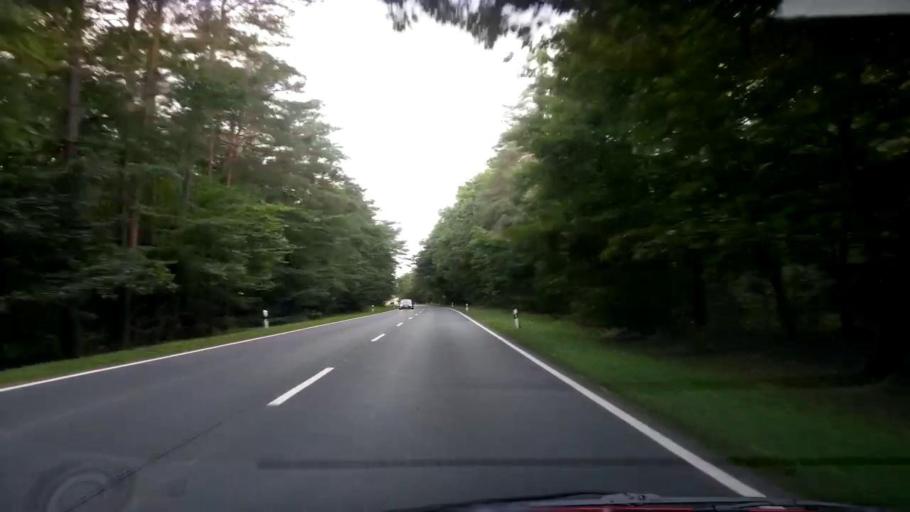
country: DE
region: Bavaria
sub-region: Regierungsbezirk Mittelfranken
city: Hemhofen
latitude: 49.6998
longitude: 10.9361
